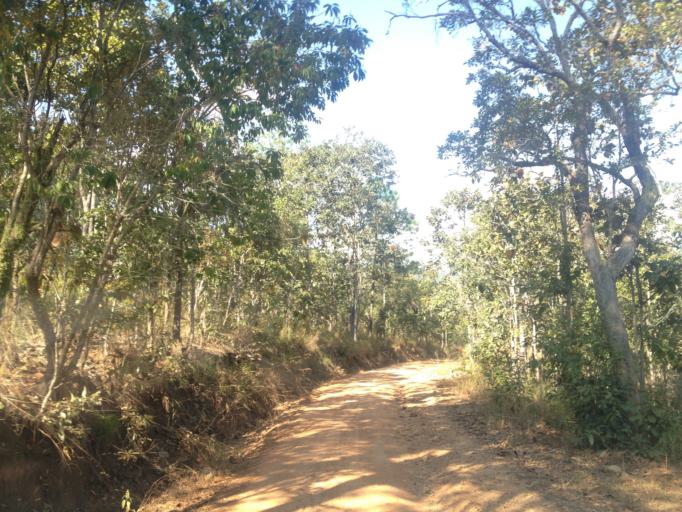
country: TH
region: Mae Hong Son
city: Ban Huai I Huak
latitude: 18.1250
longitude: 98.1995
